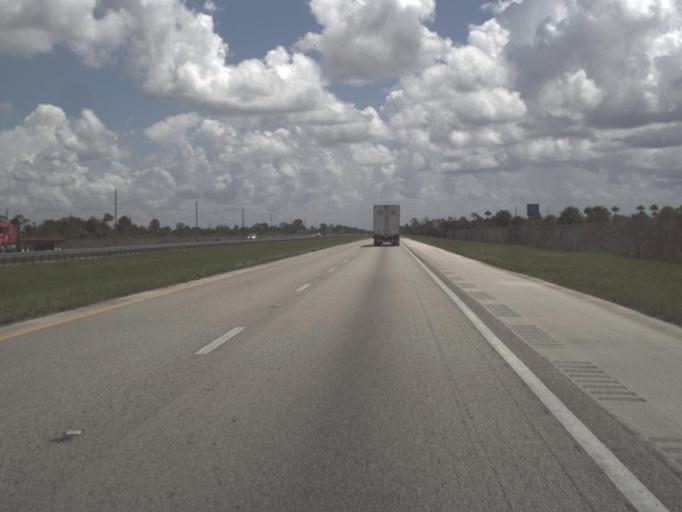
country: US
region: Florida
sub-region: Collier County
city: Immokalee
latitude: 26.1546
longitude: -81.3346
